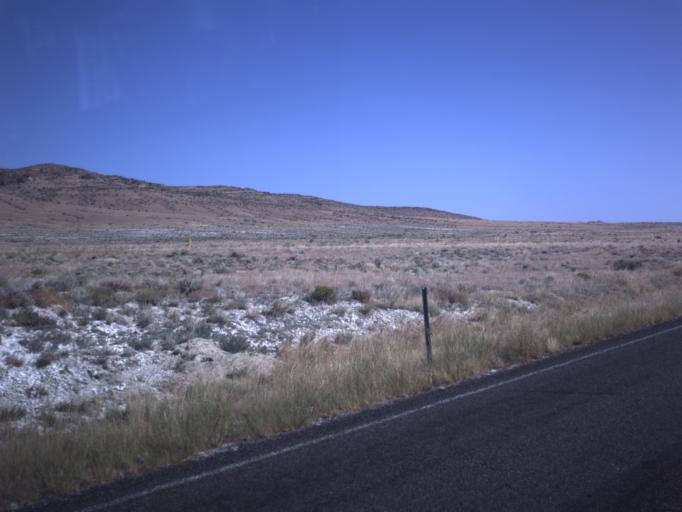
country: US
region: Utah
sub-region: Beaver County
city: Milford
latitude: 38.8713
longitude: -112.8352
